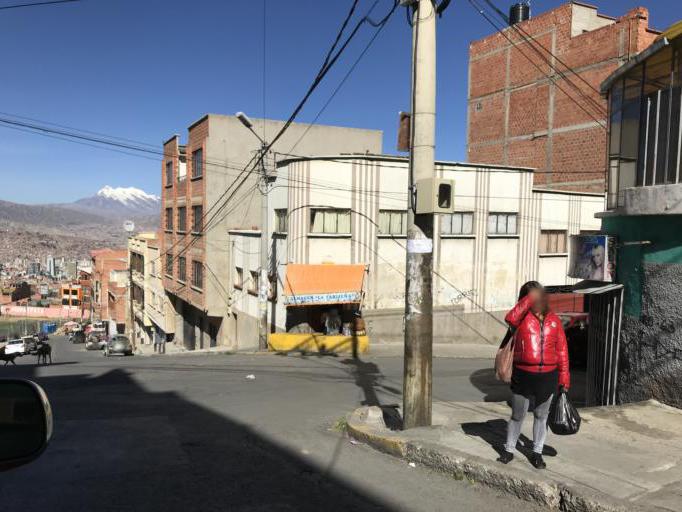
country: BO
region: La Paz
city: La Paz
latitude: -16.4881
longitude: -68.1615
